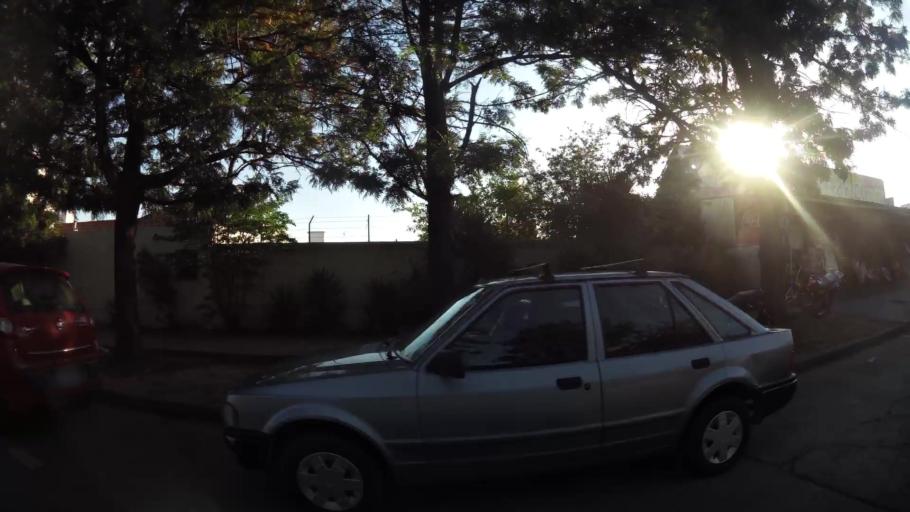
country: AR
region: Cordoba
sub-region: Departamento de Capital
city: Cordoba
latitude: -31.3833
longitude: -64.2414
